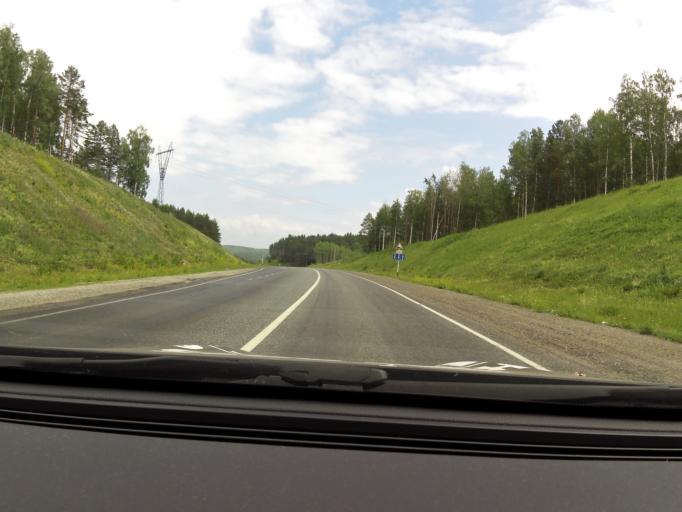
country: RU
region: Perm
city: Suksun
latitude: 57.0929
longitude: 57.3345
